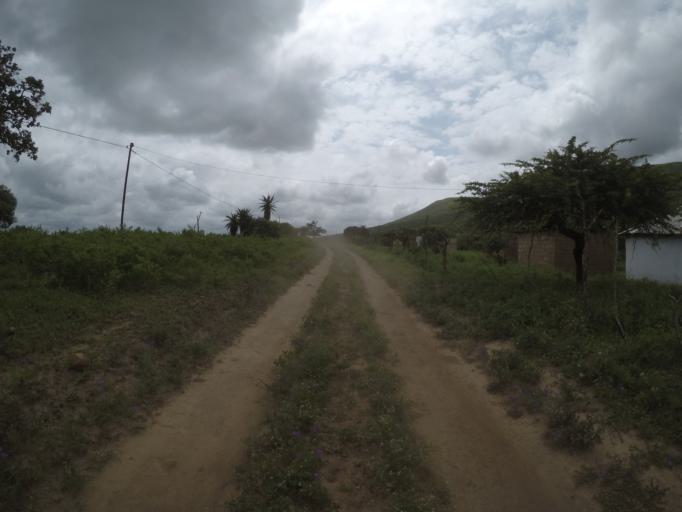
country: ZA
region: KwaZulu-Natal
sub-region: uThungulu District Municipality
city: Empangeni
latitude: -28.5803
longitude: 31.8690
